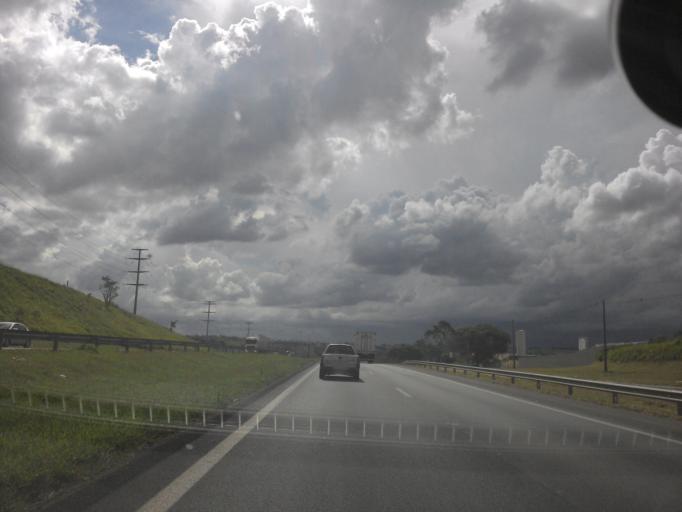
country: BR
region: Sao Paulo
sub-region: Valinhos
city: Valinhos
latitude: -22.9122
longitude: -46.9662
